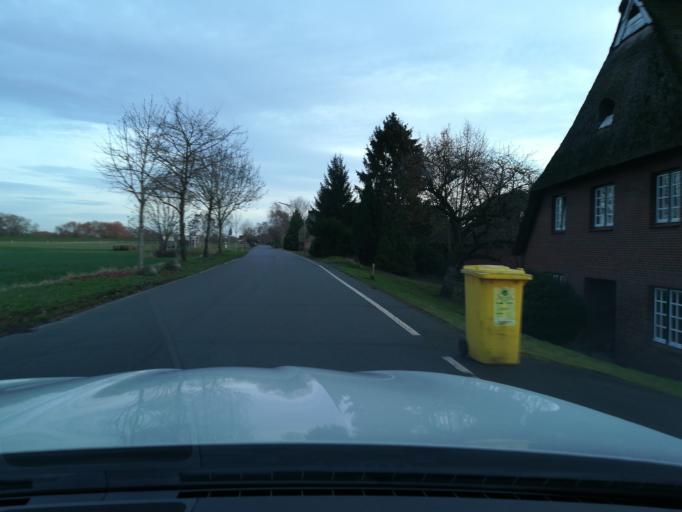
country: DE
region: Hamburg
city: Harburg
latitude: 53.4675
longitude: 10.0377
